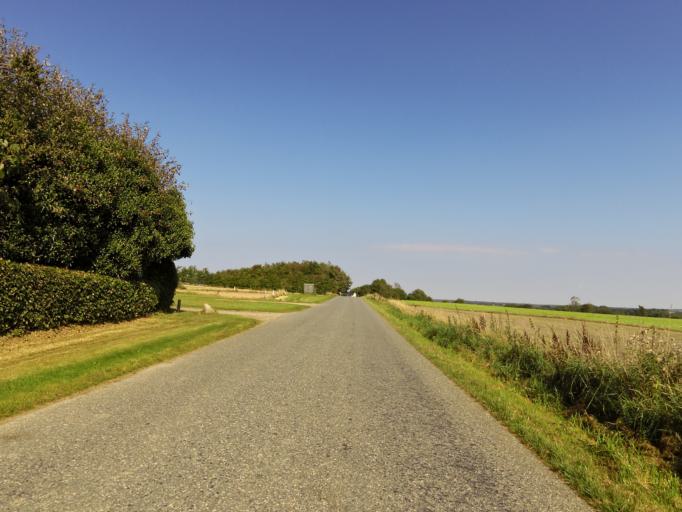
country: DK
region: South Denmark
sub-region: Vejen Kommune
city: Rodding
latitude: 55.3229
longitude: 9.1127
